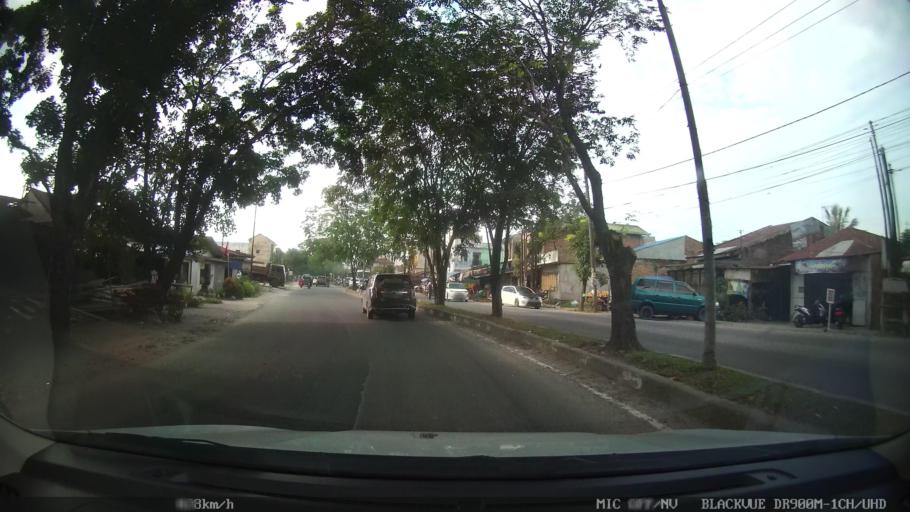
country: ID
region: North Sumatra
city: Sunggal
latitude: 3.5579
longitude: 98.6173
